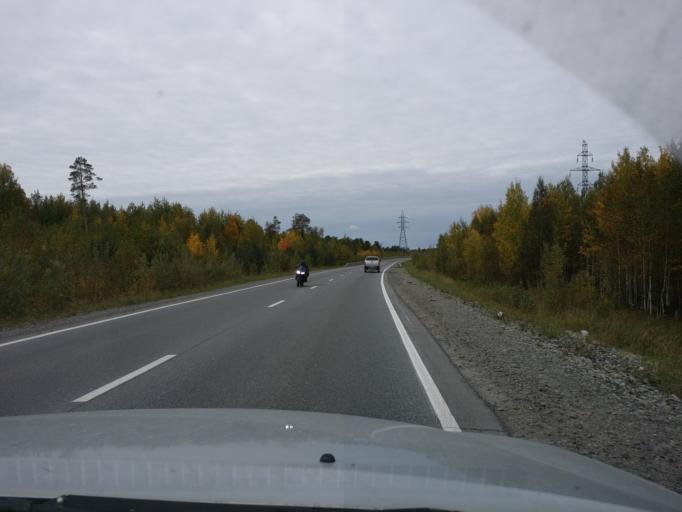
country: RU
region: Khanty-Mansiyskiy Avtonomnyy Okrug
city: Megion
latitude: 61.1024
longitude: 75.8845
